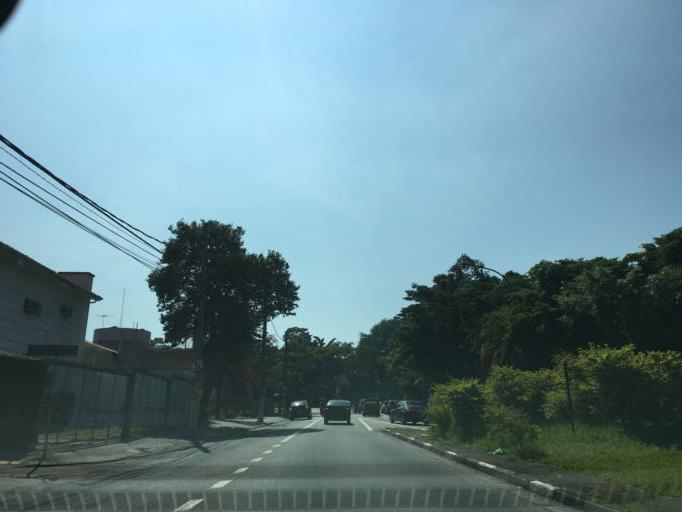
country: BR
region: Sao Paulo
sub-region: Sao Paulo
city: Sao Paulo
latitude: -23.5746
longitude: -46.7082
